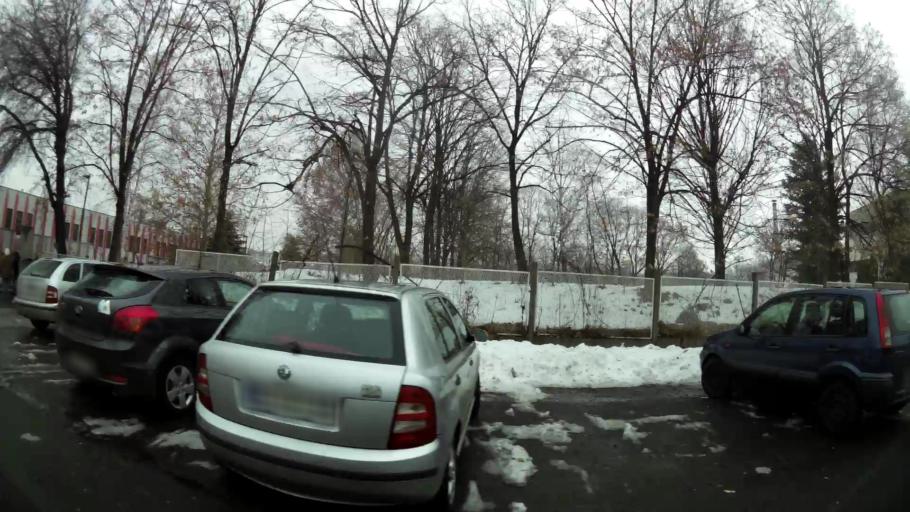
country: RS
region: Central Serbia
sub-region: Belgrade
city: Vozdovac
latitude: 44.7588
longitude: 20.4968
